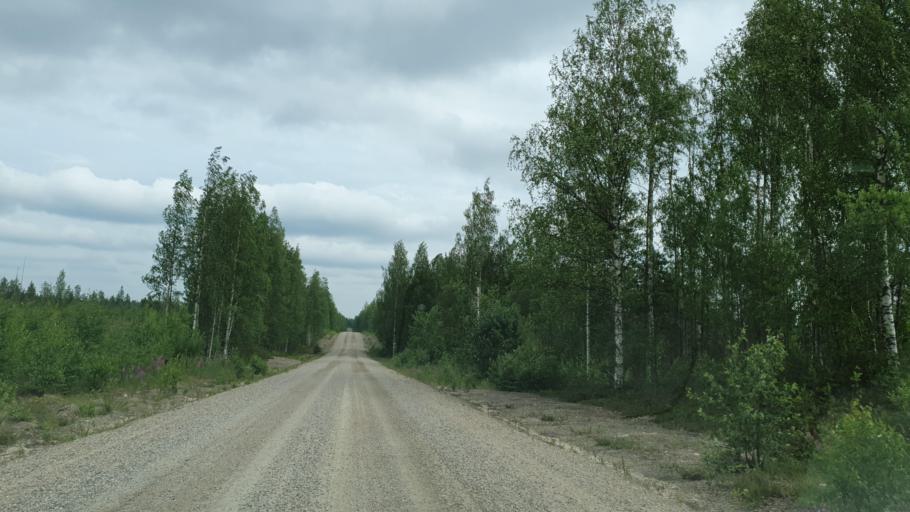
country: FI
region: Kainuu
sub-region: Kehys-Kainuu
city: Kuhmo
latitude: 63.9677
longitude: 29.3338
